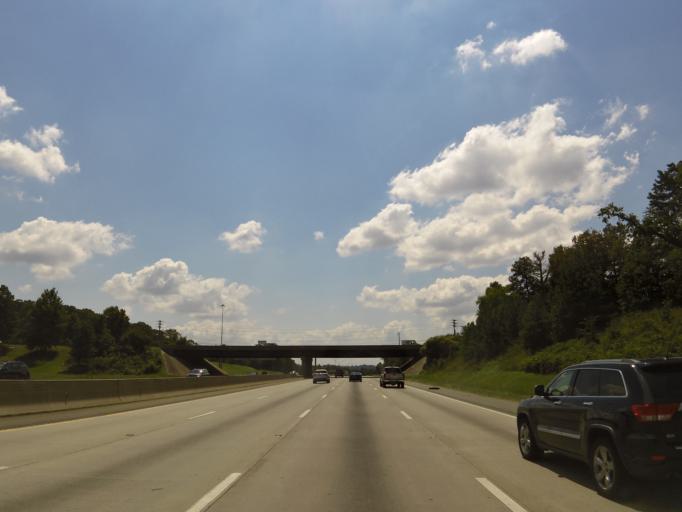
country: US
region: North Carolina
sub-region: Cabarrus County
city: Harrisburg
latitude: 35.3334
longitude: -80.7439
